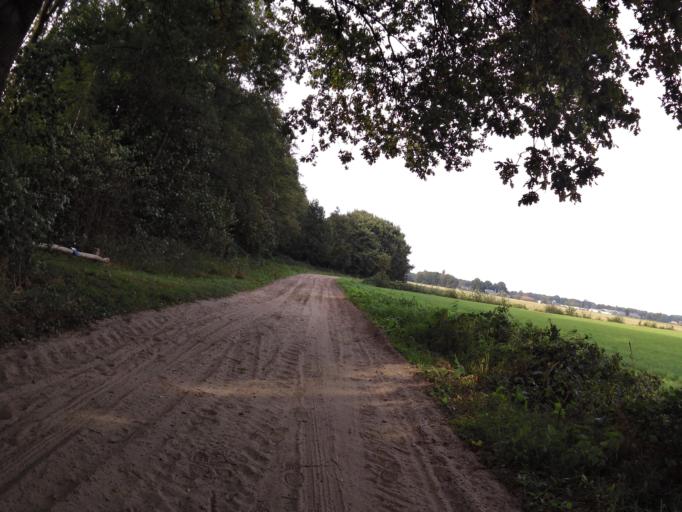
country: NL
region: North Brabant
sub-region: Gemeente Haaren
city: Haaren
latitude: 51.6059
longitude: 5.2470
